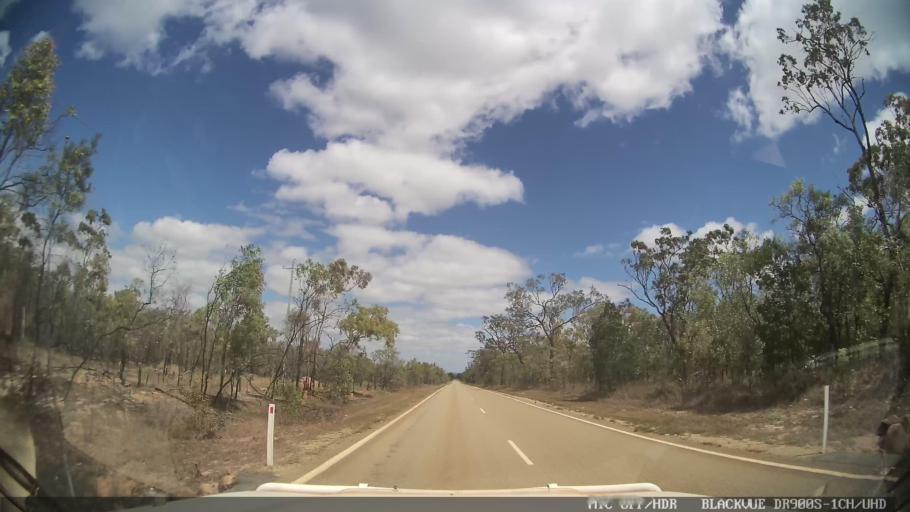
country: AU
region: Queensland
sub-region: Tablelands
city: Ravenshoe
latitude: -17.8097
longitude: 144.9584
